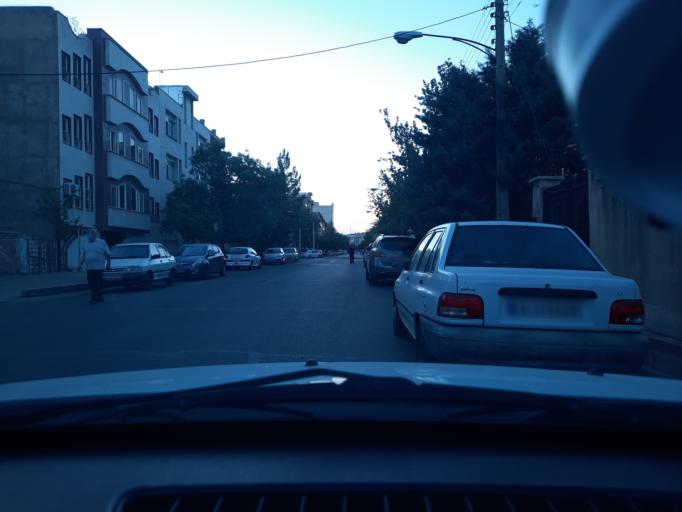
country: IR
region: Qazvin
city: Qazvin
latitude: 36.2974
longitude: 50.0183
